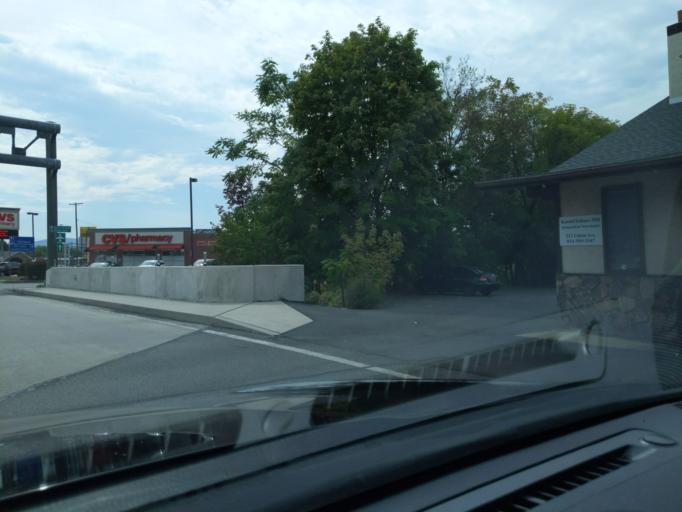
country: US
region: Pennsylvania
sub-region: Blair County
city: Lakemont
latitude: 40.4827
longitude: -78.4025
